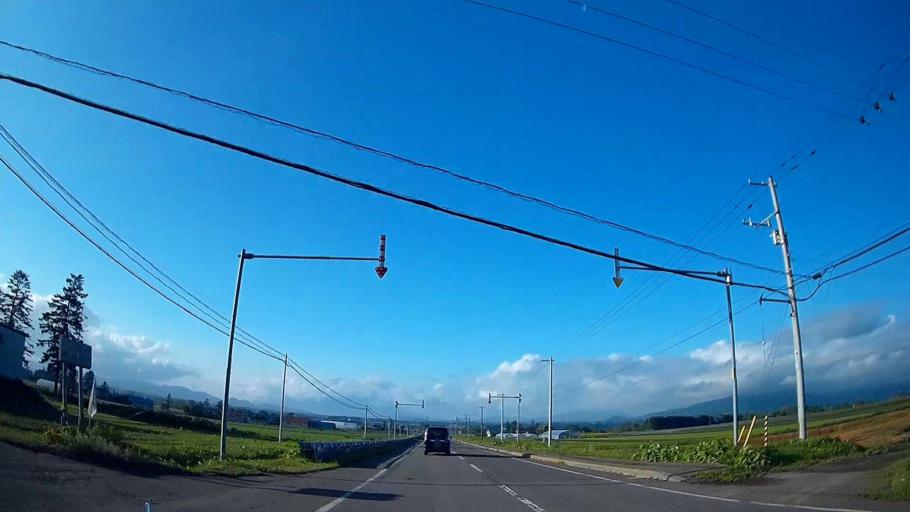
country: JP
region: Hokkaido
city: Date
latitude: 42.6308
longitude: 140.8002
